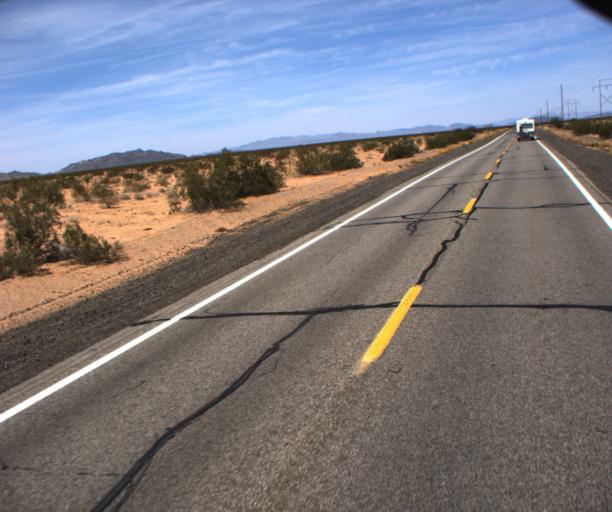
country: US
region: Arizona
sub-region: La Paz County
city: Quartzsite
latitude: 33.9110
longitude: -114.2169
